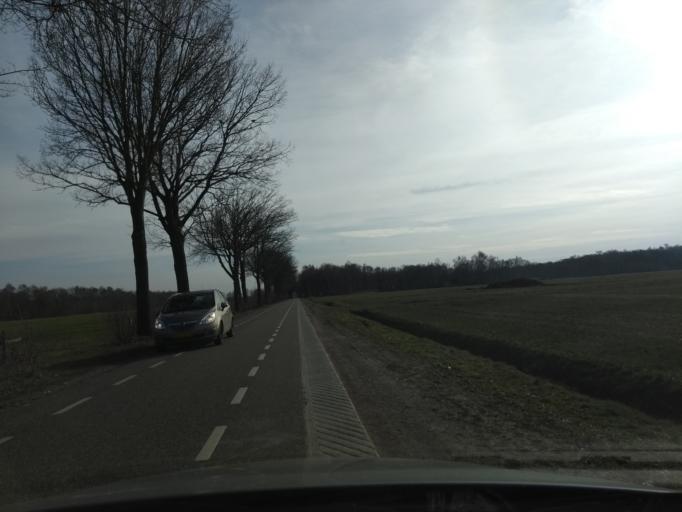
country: NL
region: Overijssel
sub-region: Gemeente Twenterand
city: Westerhaar-Vriezenveensewijk
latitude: 52.4496
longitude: 6.6540
